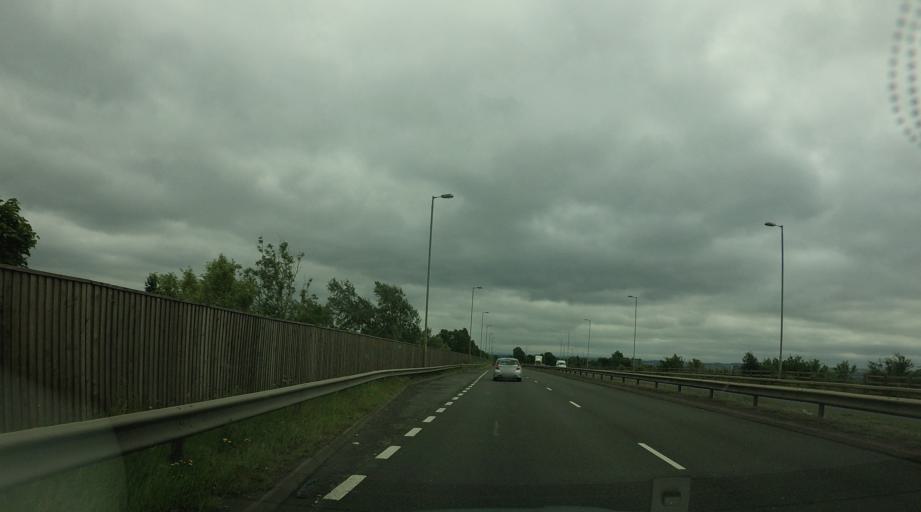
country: GB
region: Scotland
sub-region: North Lanarkshire
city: Bellshill
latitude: 55.8149
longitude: -4.0386
